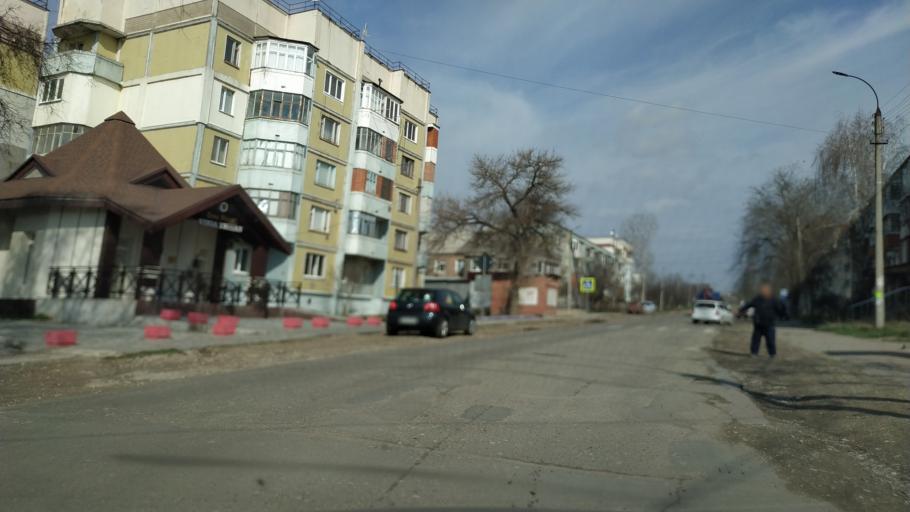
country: MD
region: Gagauzia
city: Vulcanesti
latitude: 45.6872
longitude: 28.4039
